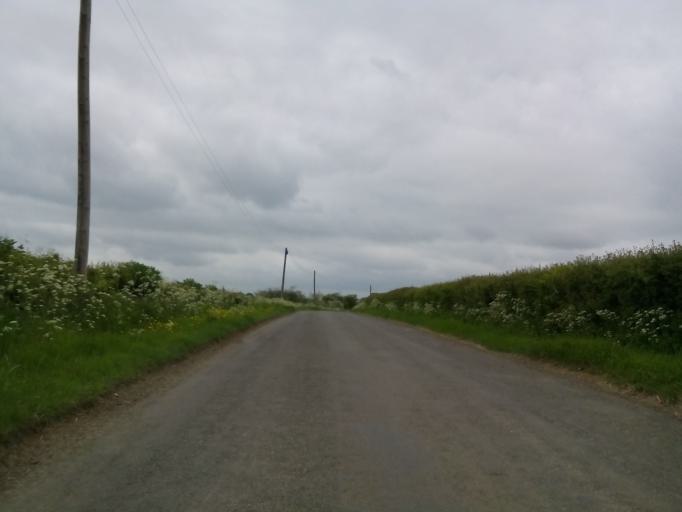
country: GB
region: England
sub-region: Northamptonshire
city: Oundle
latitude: 52.5163
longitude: -0.5058
